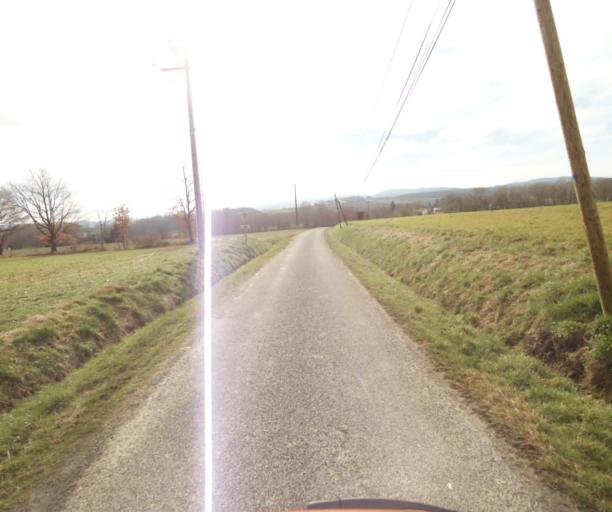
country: FR
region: Midi-Pyrenees
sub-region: Departement de l'Ariege
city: Pamiers
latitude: 43.1073
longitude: 1.5346
